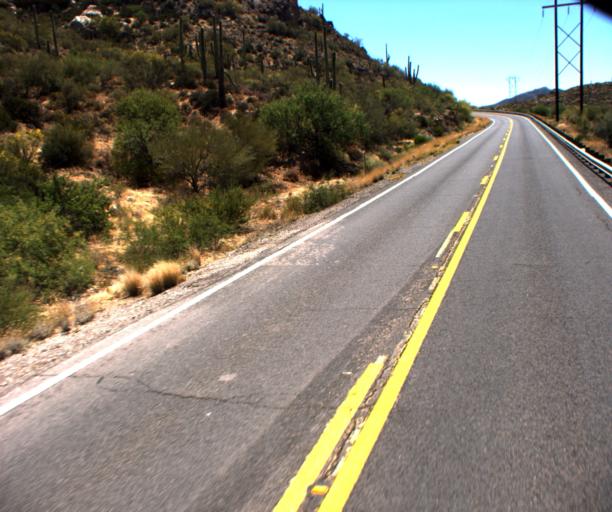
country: US
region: Arizona
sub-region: Pinal County
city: Superior
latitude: 33.2341
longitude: -111.0929
